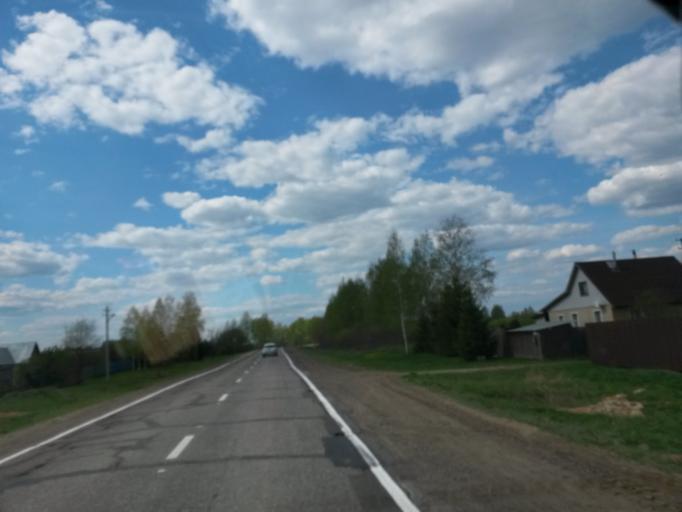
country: RU
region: Jaroslavl
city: Bol'shoye Selo
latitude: 57.6873
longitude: 39.2055
